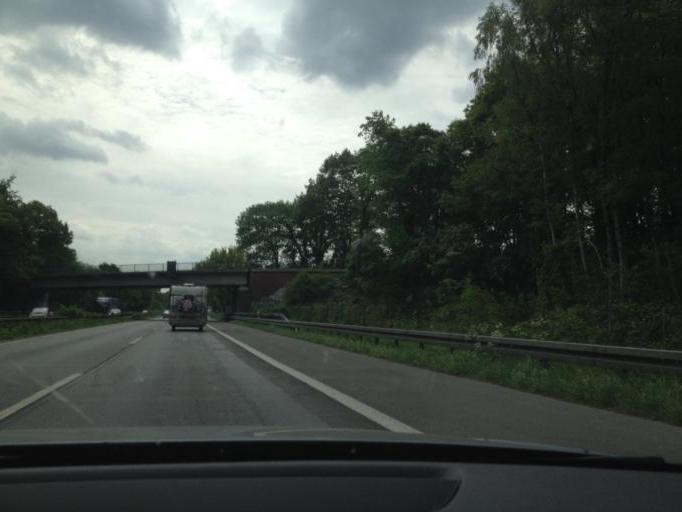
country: DE
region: North Rhine-Westphalia
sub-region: Regierungsbezirk Dusseldorf
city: Dinslaken
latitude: 51.5811
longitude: 6.7920
